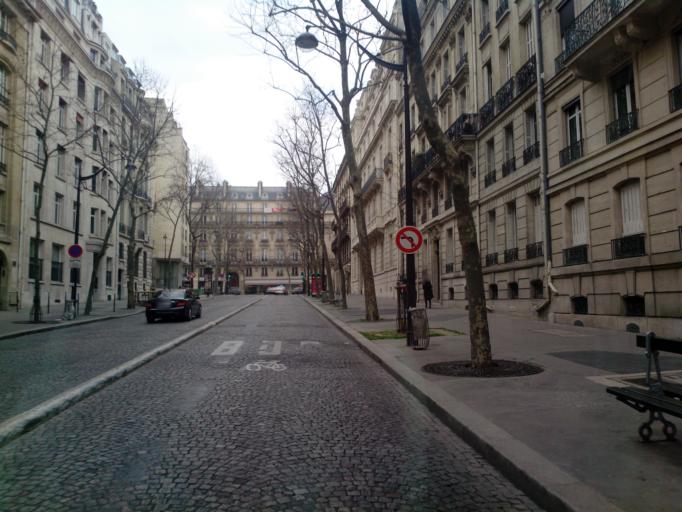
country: FR
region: Ile-de-France
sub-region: Departement des Hauts-de-Seine
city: Clichy
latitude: 48.8740
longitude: 2.3145
